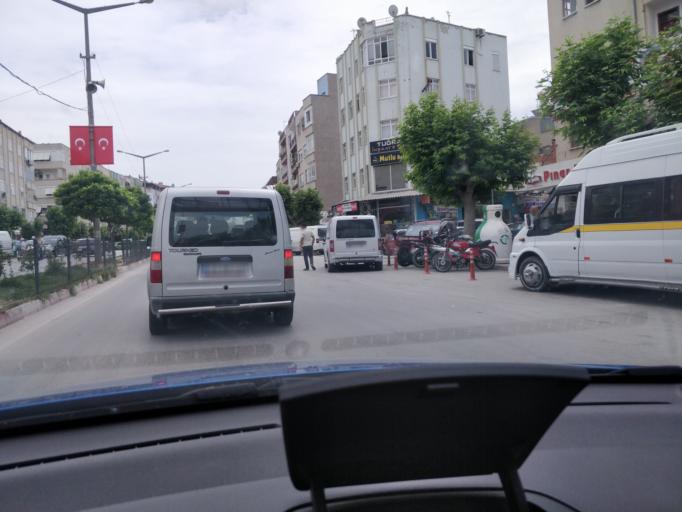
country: TR
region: Mersin
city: Mut
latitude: 36.6452
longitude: 33.4373
